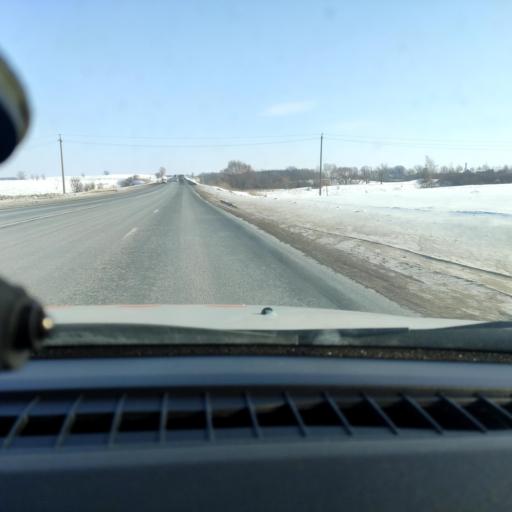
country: RU
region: Samara
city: Novosemeykino
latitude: 53.4010
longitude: 50.4043
